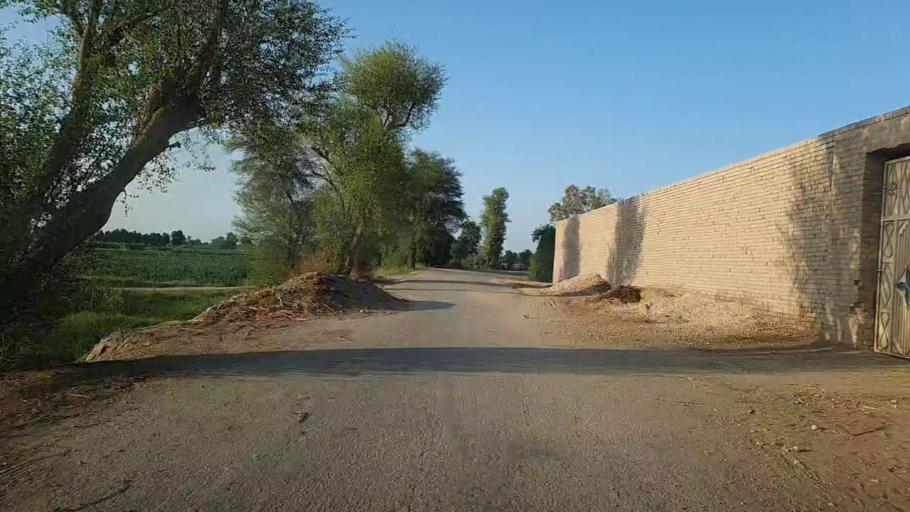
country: PK
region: Sindh
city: Bhan
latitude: 26.5814
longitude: 67.7606
